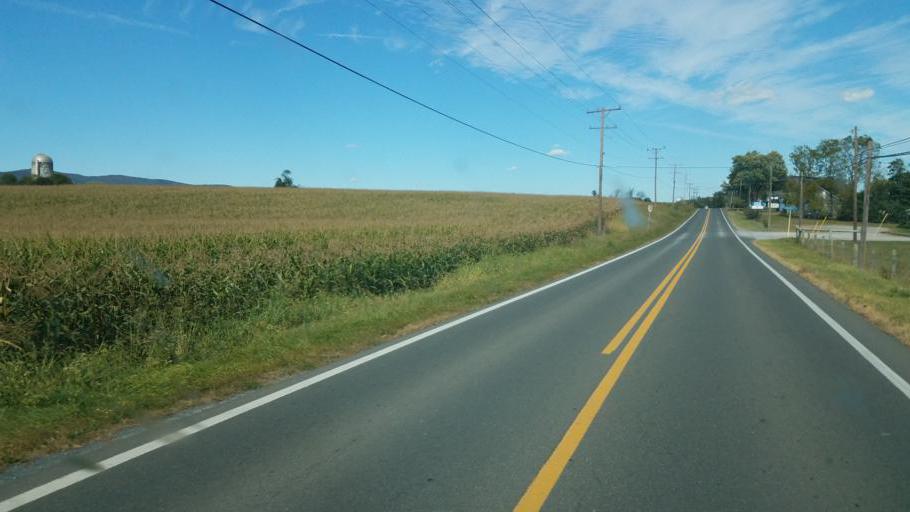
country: US
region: Virginia
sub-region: Page County
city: Luray
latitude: 38.6936
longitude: -78.4499
